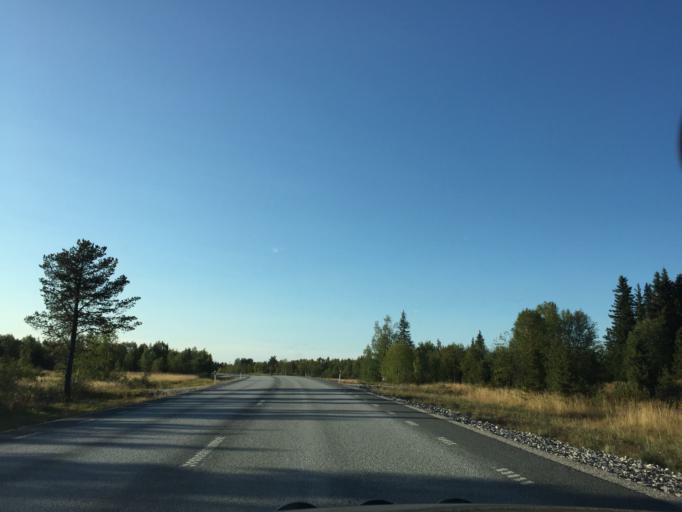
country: SE
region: Norrbotten
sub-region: Gallivare Kommun
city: Malmberget
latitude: 67.6414
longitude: 21.0588
